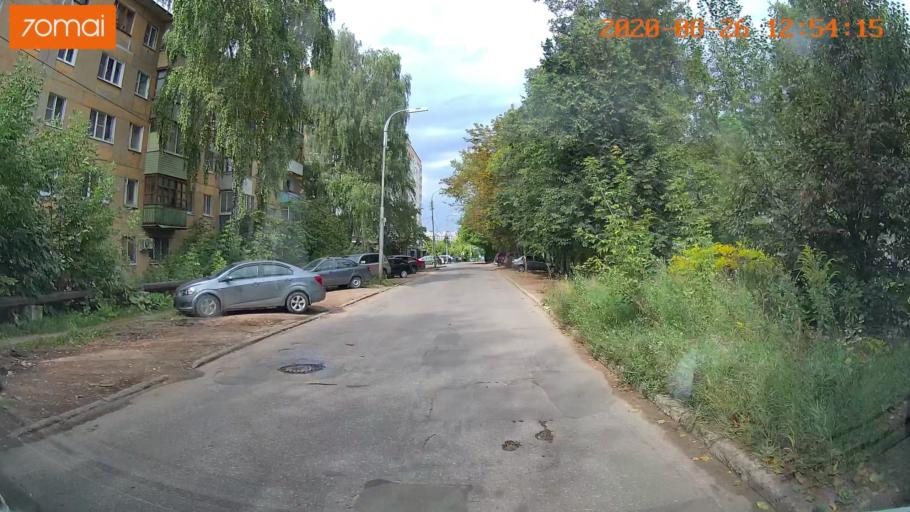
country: RU
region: Rjazan
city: Ryazan'
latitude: 54.6036
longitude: 39.7590
